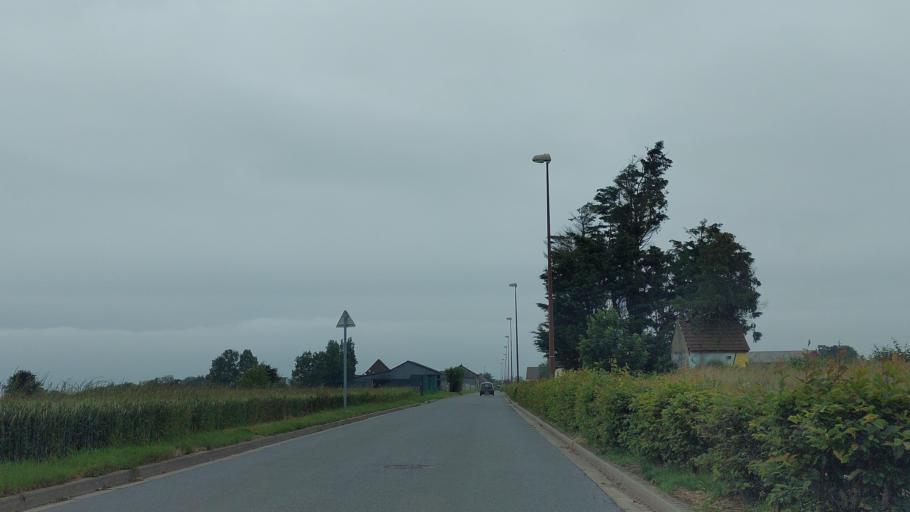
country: FR
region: Picardie
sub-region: Departement de la Somme
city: Ault
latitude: 50.0976
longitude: 1.4610
